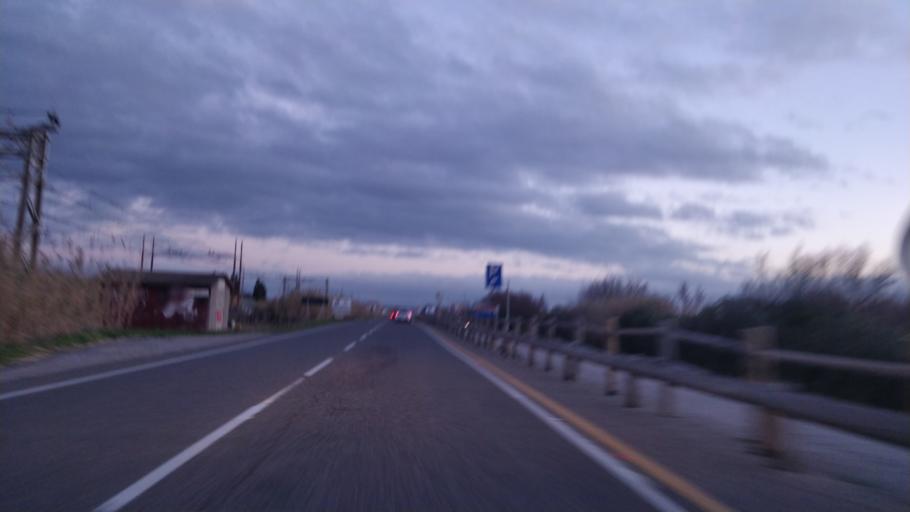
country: IT
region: Tuscany
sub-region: Provincia di Livorno
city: Rosignano Solvay-Castiglioncello
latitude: 43.3777
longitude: 10.4459
